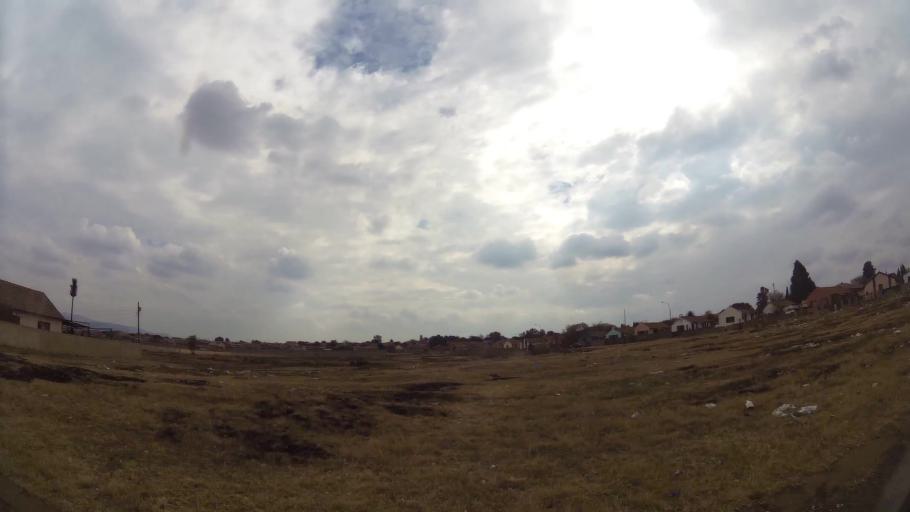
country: ZA
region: Gauteng
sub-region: Ekurhuleni Metropolitan Municipality
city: Germiston
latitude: -26.3852
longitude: 28.1303
